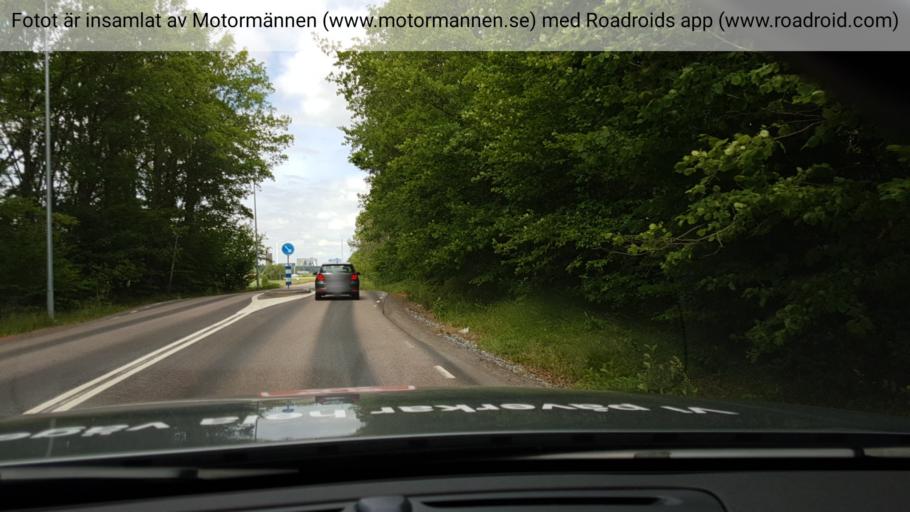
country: SE
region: Vaestmanland
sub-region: Vasteras
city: Vasteras
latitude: 59.5666
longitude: 16.5236
